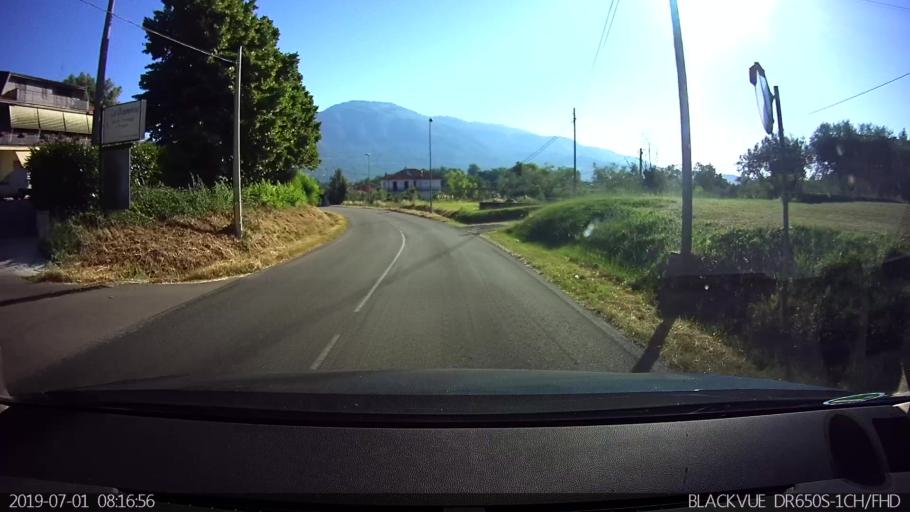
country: IT
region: Latium
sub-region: Provincia di Frosinone
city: Veroli
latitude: 41.7015
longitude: 13.4350
